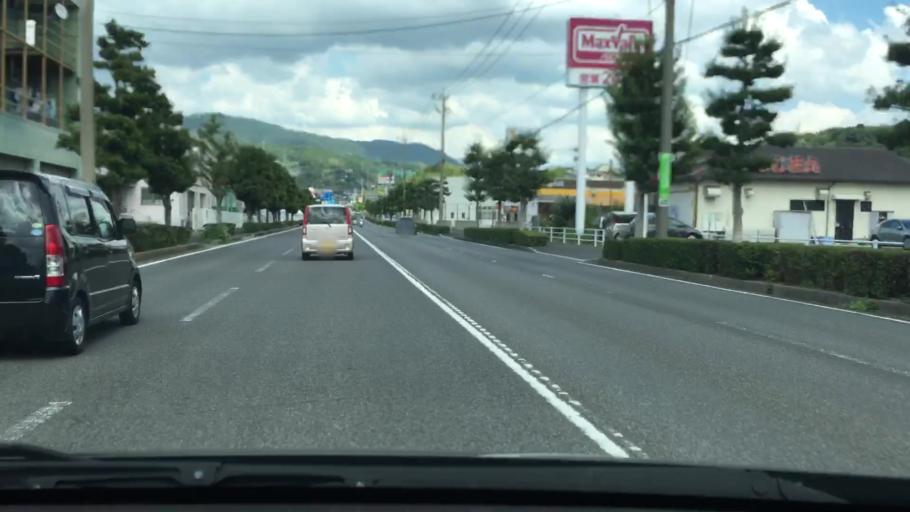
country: JP
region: Nagasaki
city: Sasebo
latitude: 33.2082
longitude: 129.6921
